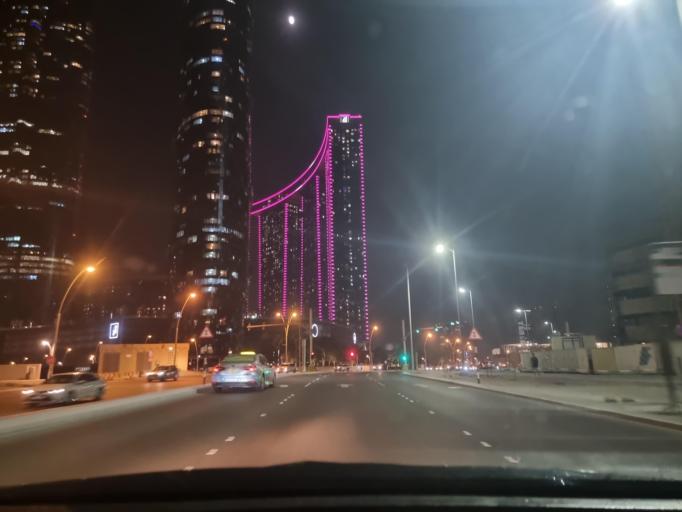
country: AE
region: Abu Dhabi
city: Abu Dhabi
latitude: 24.4975
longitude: 54.4052
